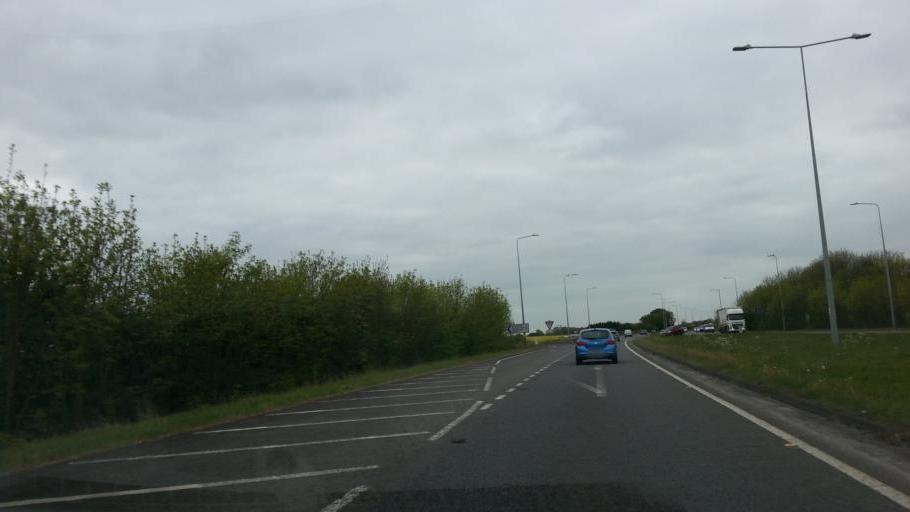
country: GB
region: England
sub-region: Lincolnshire
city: Heckington
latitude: 52.9873
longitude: -0.3201
